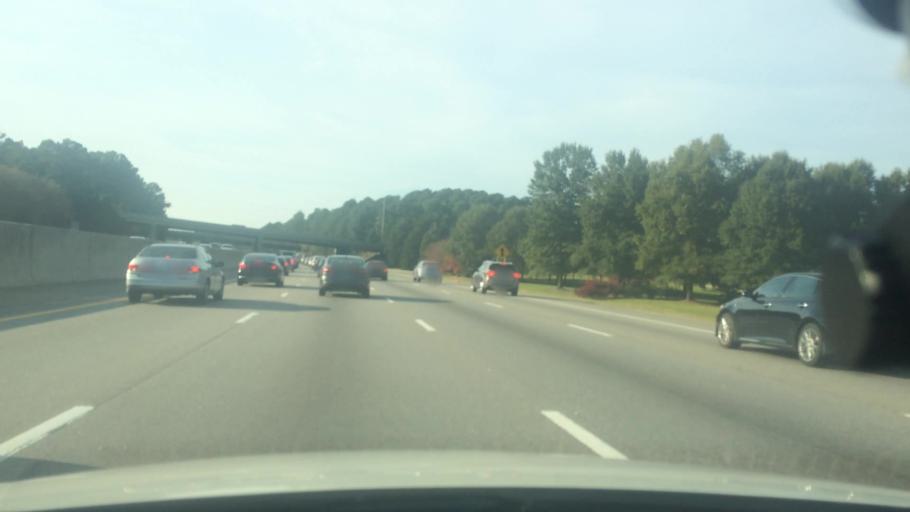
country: US
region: North Carolina
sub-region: Wake County
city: Morrisville
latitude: 35.8894
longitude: -78.8465
